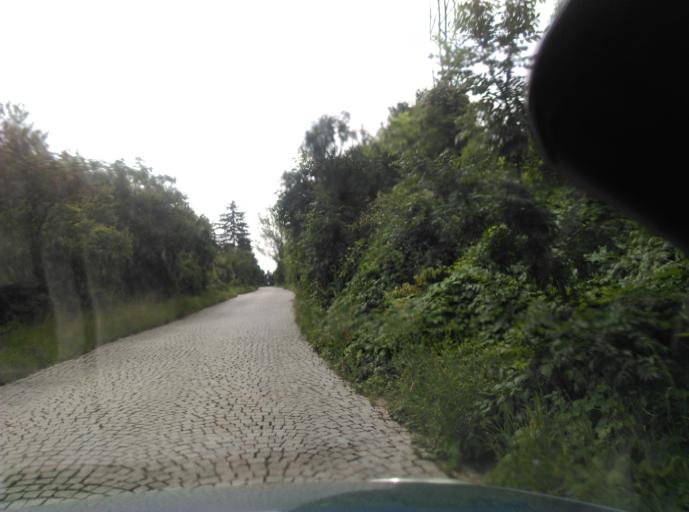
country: BG
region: Sofia-Capital
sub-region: Stolichna Obshtina
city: Sofia
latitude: 42.6057
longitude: 23.3975
